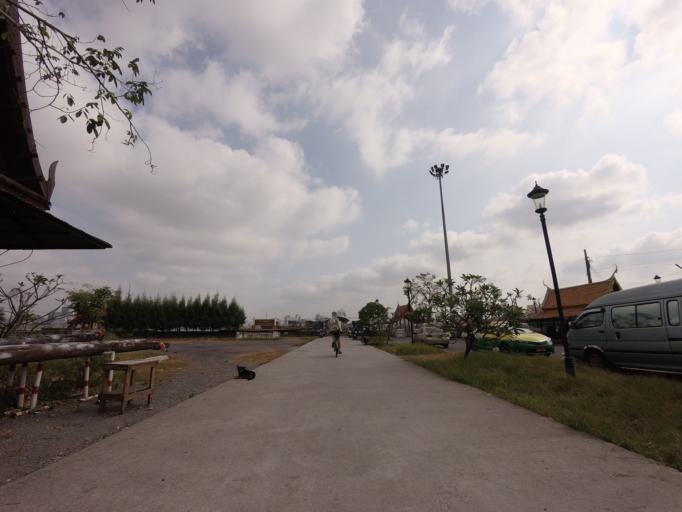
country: TH
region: Bangkok
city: Khlong Toei
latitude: 13.6978
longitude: 100.5770
